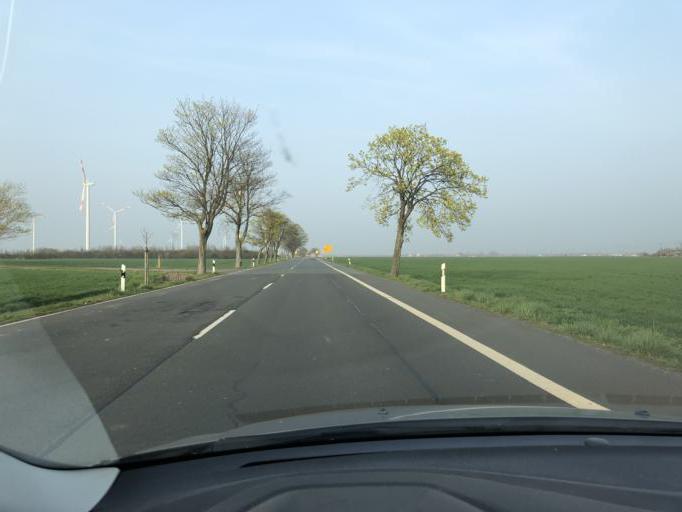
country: DE
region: Saxony-Anhalt
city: Brehna
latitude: 51.5648
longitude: 12.2187
